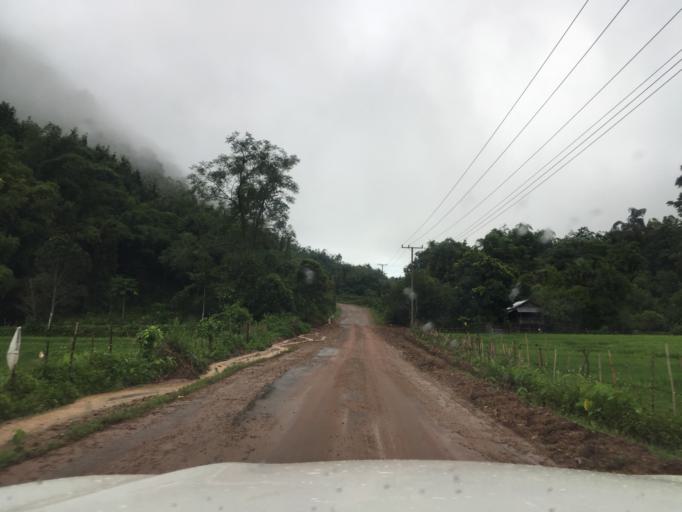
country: LA
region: Oudomxai
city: Muang La
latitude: 20.8301
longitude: 102.0985
